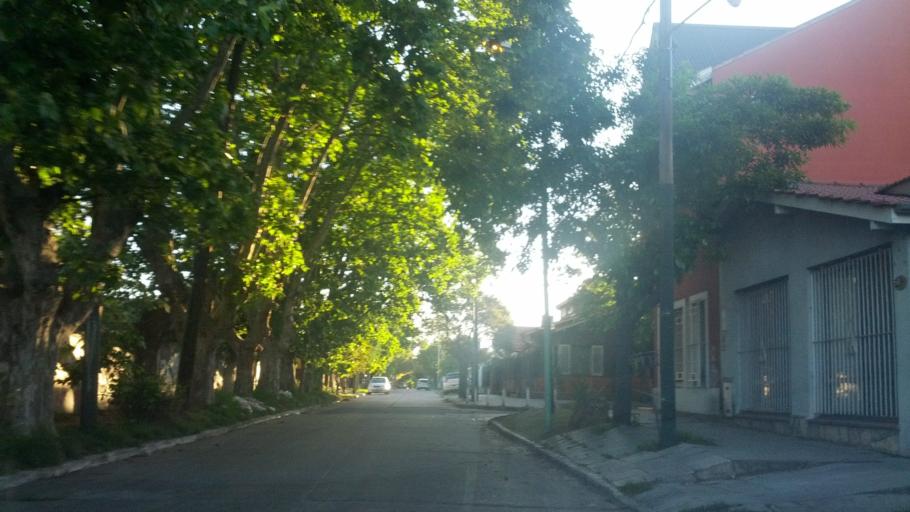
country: AR
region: Buenos Aires
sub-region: Partido de Almirante Brown
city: Adrogue
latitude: -34.7841
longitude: -58.3894
